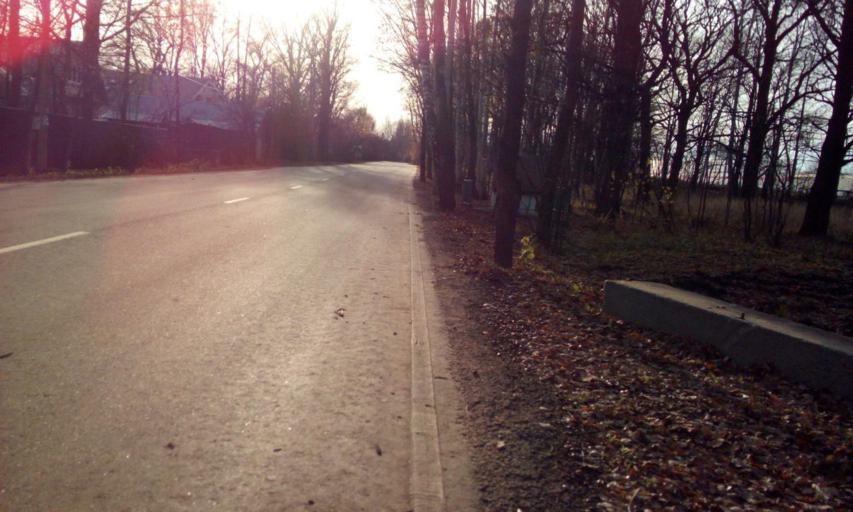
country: RU
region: Moskovskaya
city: Aprelevka
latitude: 55.5802
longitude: 37.1179
